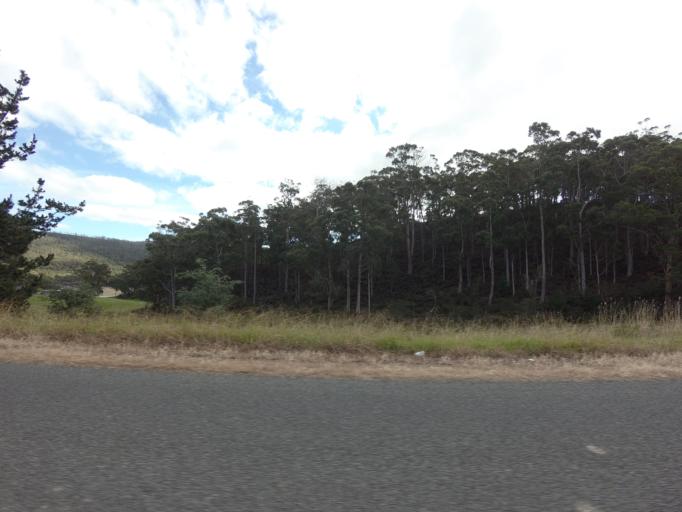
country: AU
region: Tasmania
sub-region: Clarence
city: Sandford
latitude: -43.0794
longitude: 147.7450
